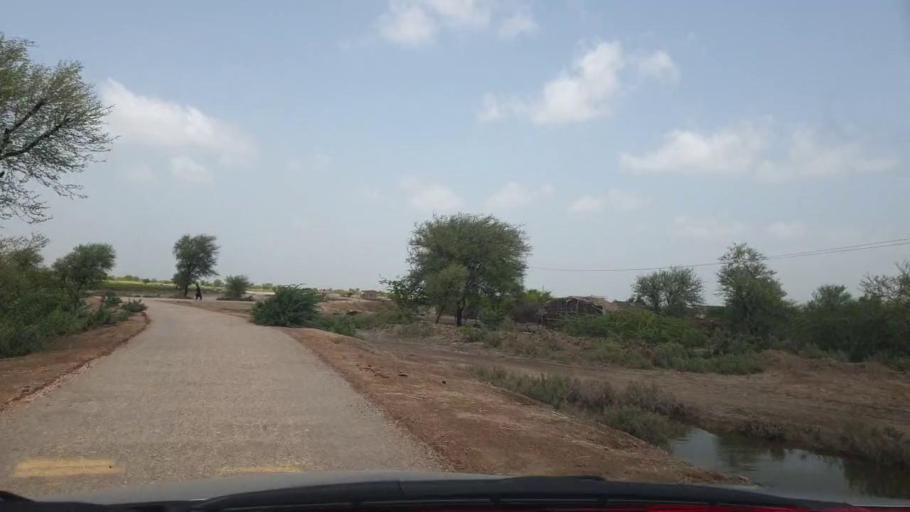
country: PK
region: Sindh
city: Rajo Khanani
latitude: 24.9204
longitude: 68.8983
